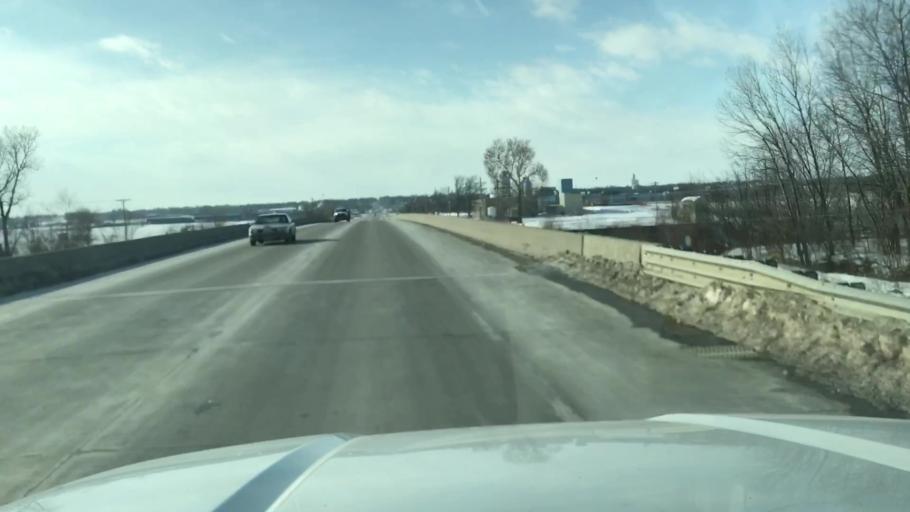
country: US
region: Missouri
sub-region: Nodaway County
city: Maryville
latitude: 40.3449
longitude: -94.8301
